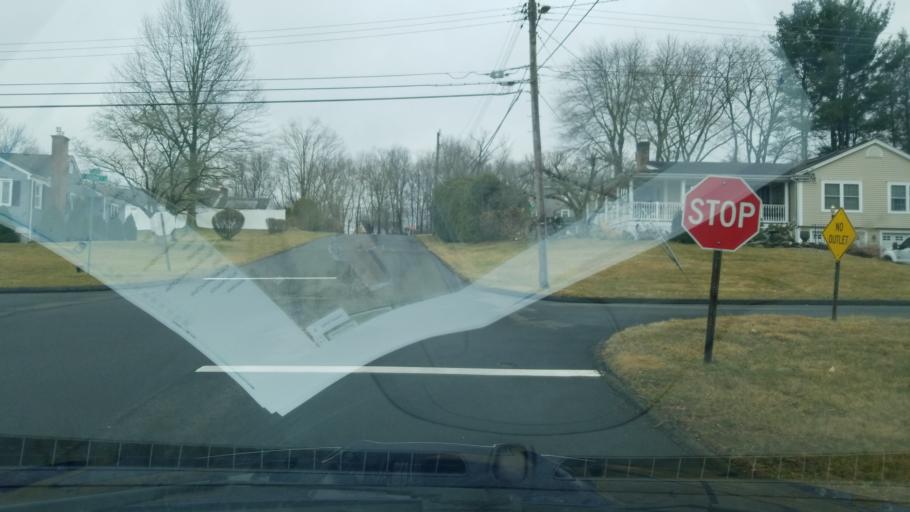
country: US
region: Connecticut
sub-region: Hartford County
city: Wethersfield
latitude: 41.6709
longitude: -72.6712
